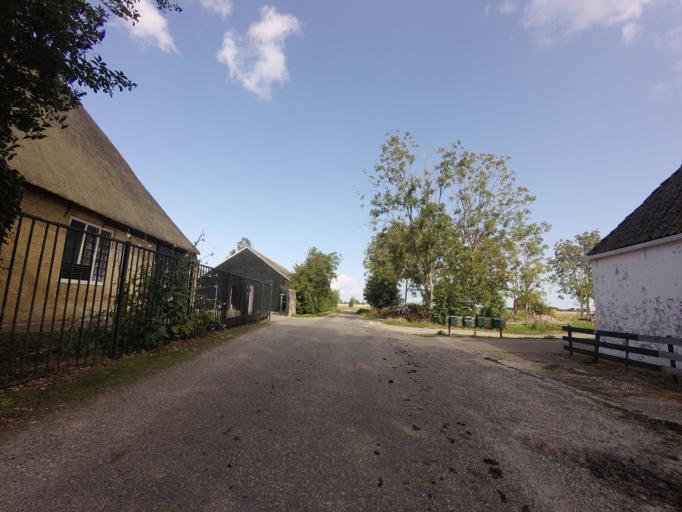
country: NL
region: Friesland
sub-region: Gemeente Franekeradeel
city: Tzummarum
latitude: 53.2424
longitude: 5.5410
